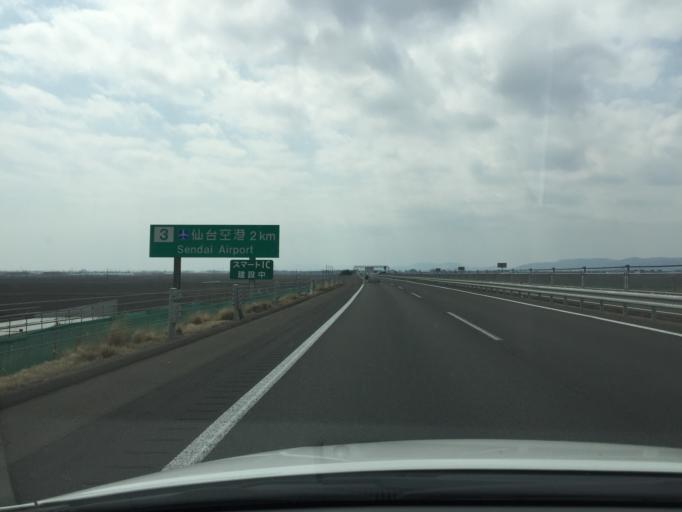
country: JP
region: Miyagi
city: Iwanuma
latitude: 38.1540
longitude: 140.8967
